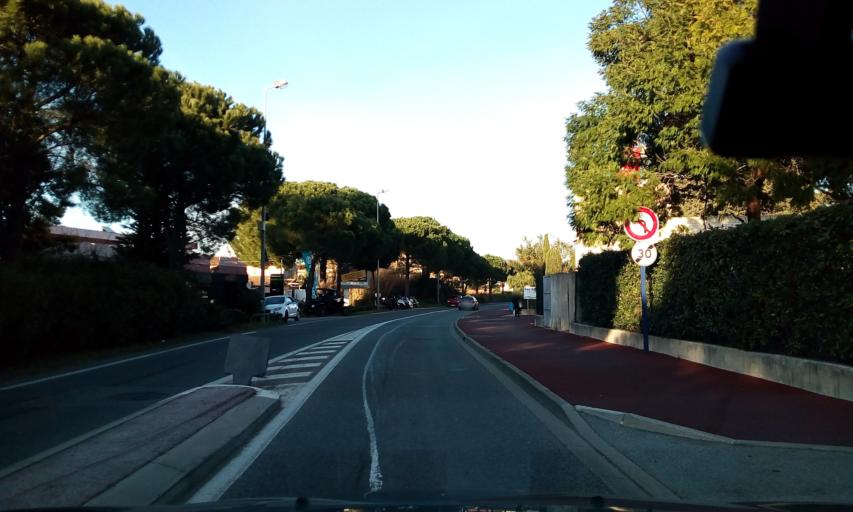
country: FR
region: Provence-Alpes-Cote d'Azur
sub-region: Departement du Var
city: Frejus
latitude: 43.4259
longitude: 6.7335
